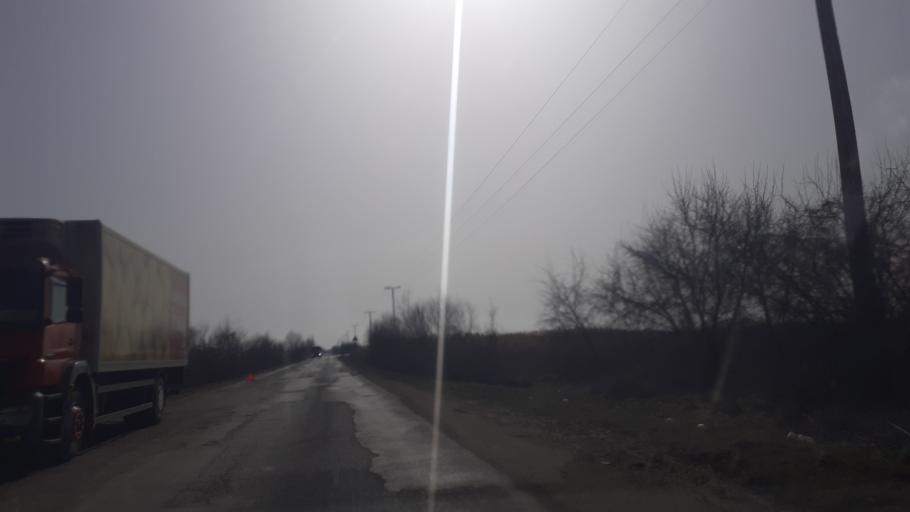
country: HU
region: Pest
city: Bugyi
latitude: 47.2143
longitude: 19.1483
